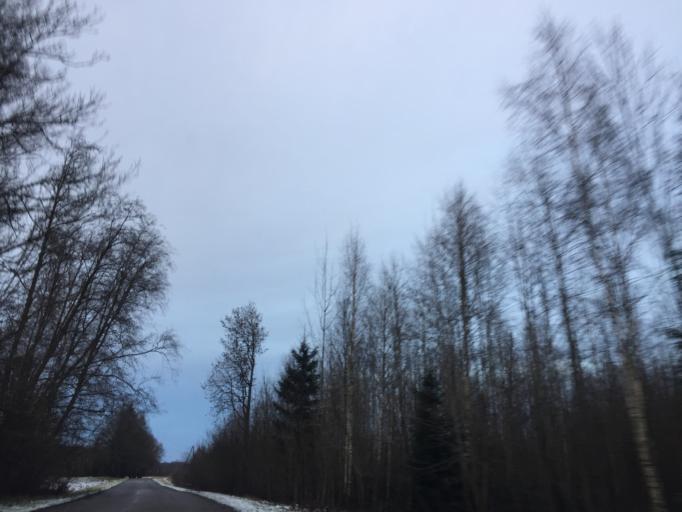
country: LV
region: Aloja
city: Aloja
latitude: 57.6314
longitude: 24.9363
